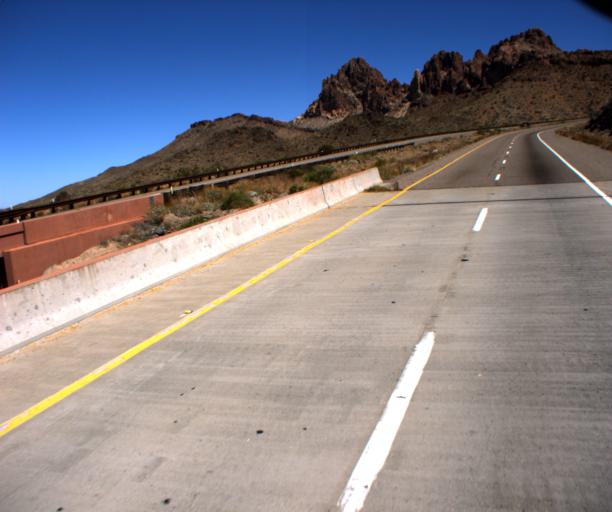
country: US
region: Nevada
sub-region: Clark County
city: Laughlin
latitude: 35.2062
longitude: -114.4032
